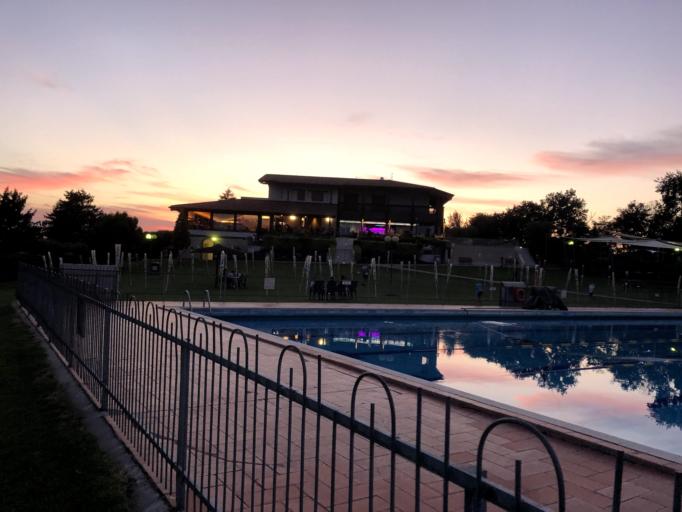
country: IT
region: Veneto
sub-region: Provincia di Verona
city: Rosegaferro
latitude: 45.3769
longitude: 10.7917
